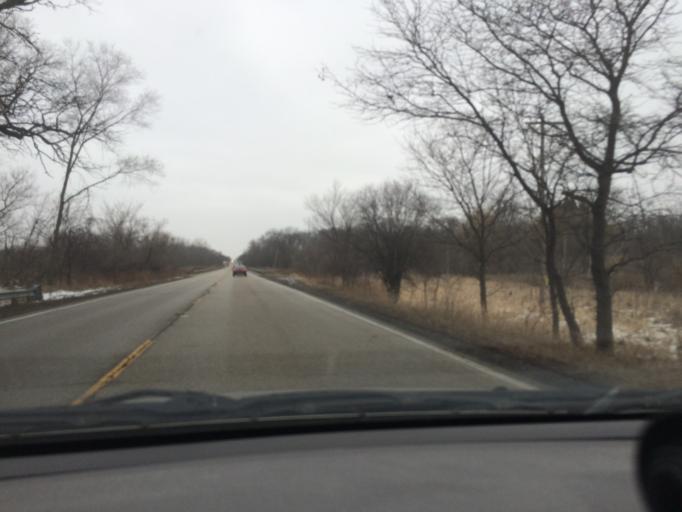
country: US
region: Illinois
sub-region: Cook County
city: Streamwood
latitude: 42.0464
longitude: -88.1528
